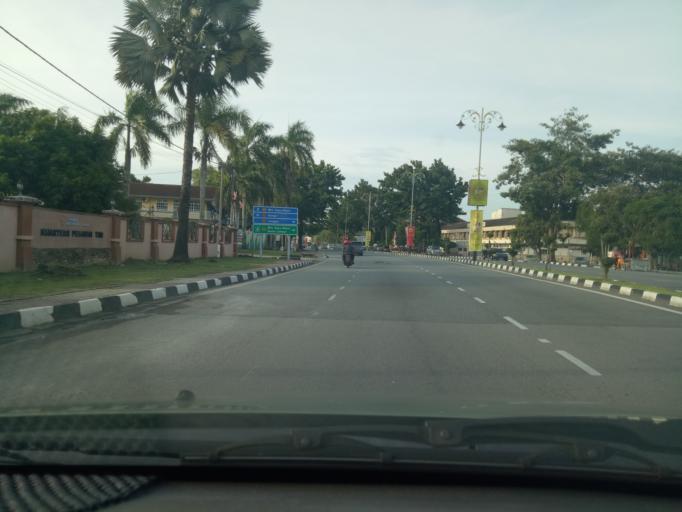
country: MY
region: Kedah
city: Alor Setar
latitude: 6.1400
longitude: 100.3704
